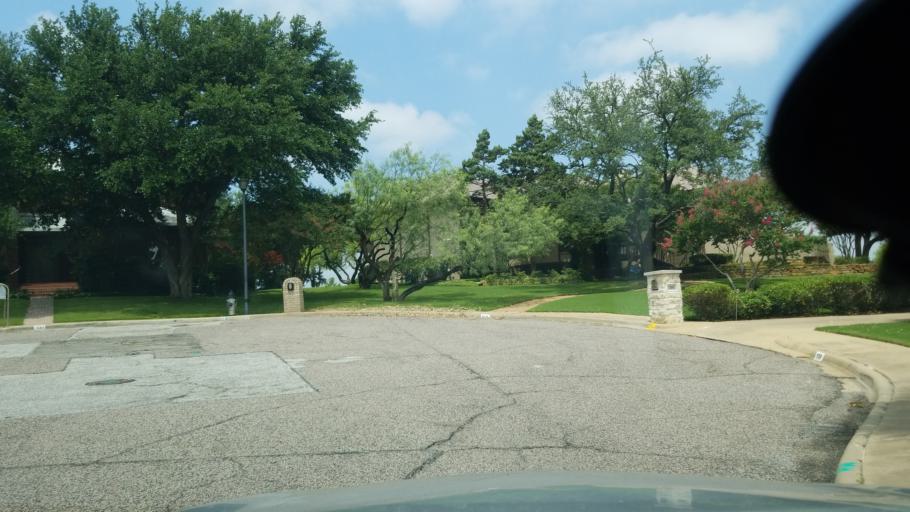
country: US
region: Texas
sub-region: Dallas County
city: Irving
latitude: 32.8575
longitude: -96.9419
